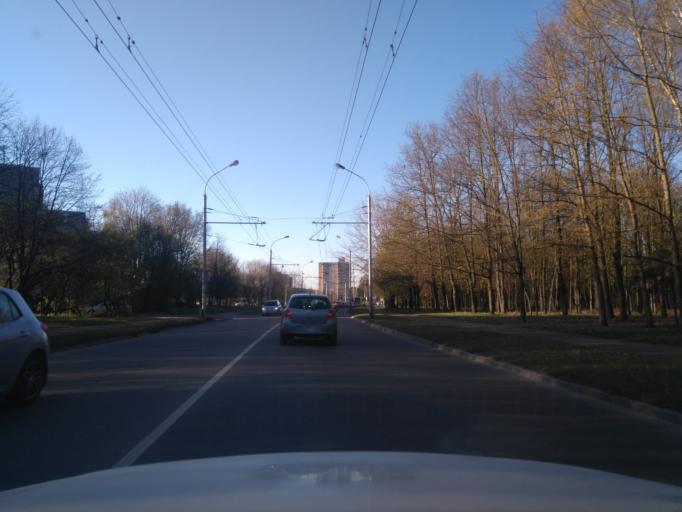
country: LT
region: Kauno apskritis
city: Dainava (Kaunas)
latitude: 54.9156
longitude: 23.9737
